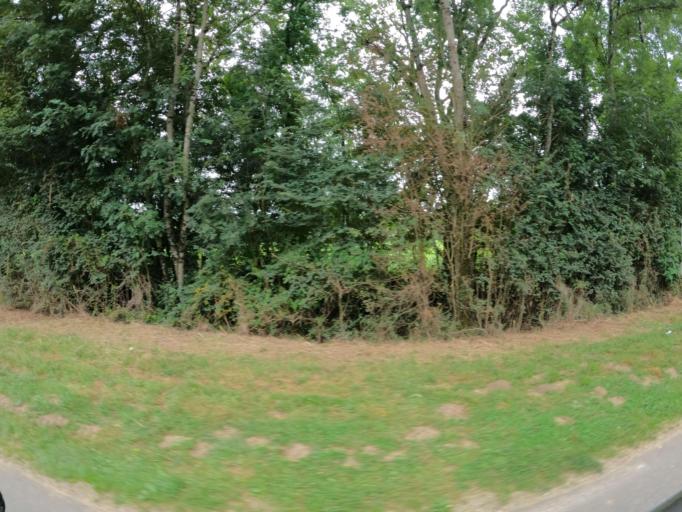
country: FR
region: Poitou-Charentes
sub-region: Departement de la Charente
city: Confolens
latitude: 45.9936
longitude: 0.6725
